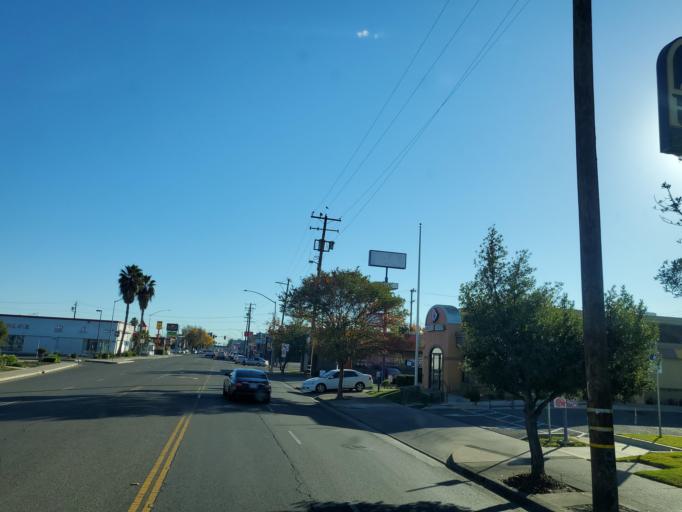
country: US
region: California
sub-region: San Joaquin County
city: Stockton
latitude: 37.9625
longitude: -121.2734
